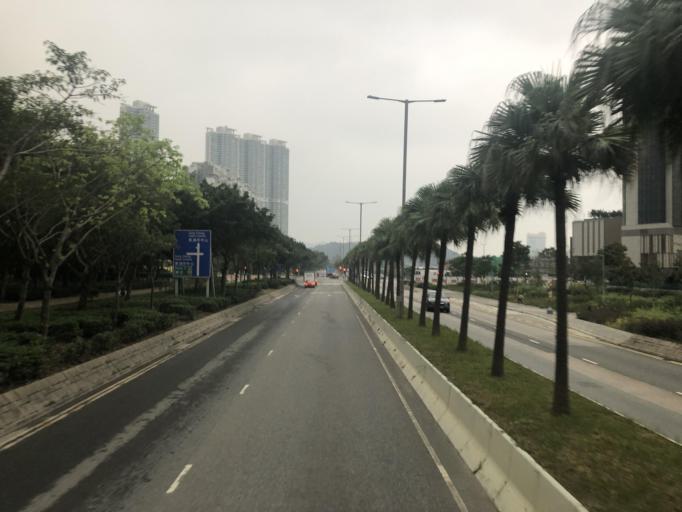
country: HK
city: Tai O
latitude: 22.2942
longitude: 113.9484
